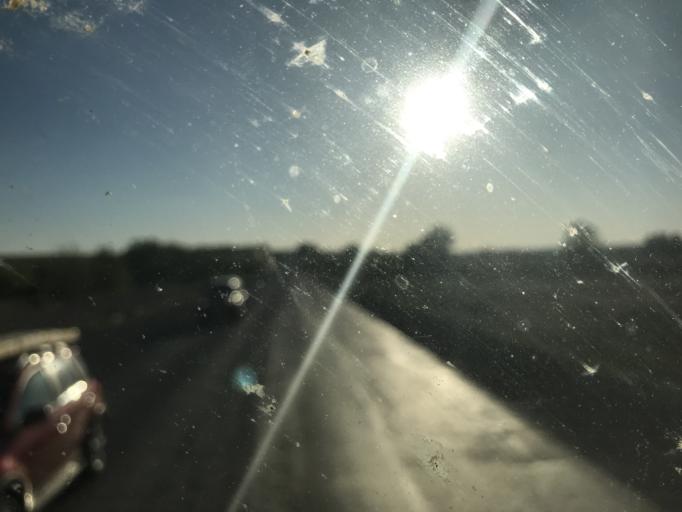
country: KZ
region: Aqtoebe
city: Aqtobe
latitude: 50.2900
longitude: 57.6803
